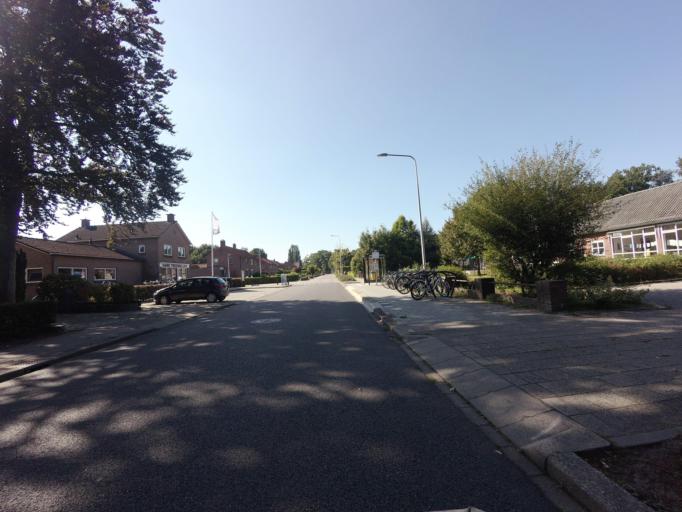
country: NL
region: Overijssel
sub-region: Gemeente Hardenberg
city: Hardenberg
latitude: 52.5282
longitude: 6.6181
